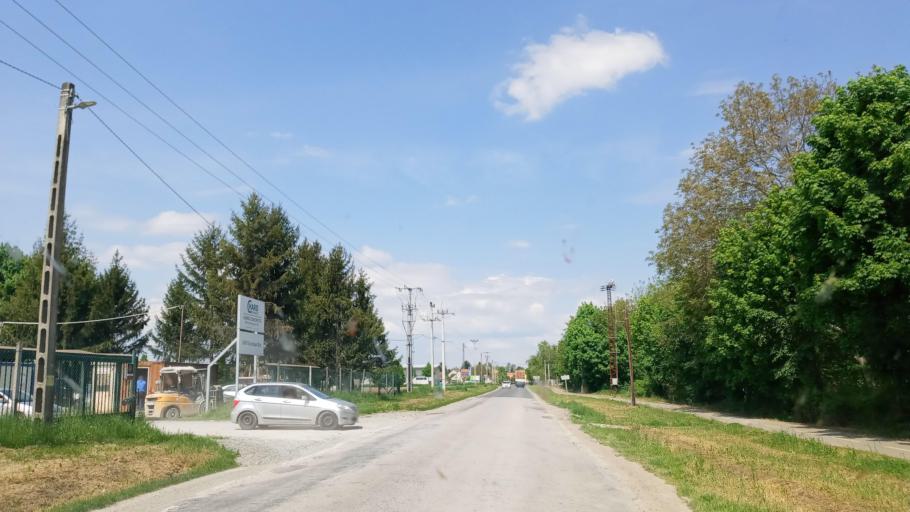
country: HU
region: Baranya
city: Boly
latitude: 45.9590
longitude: 18.5258
